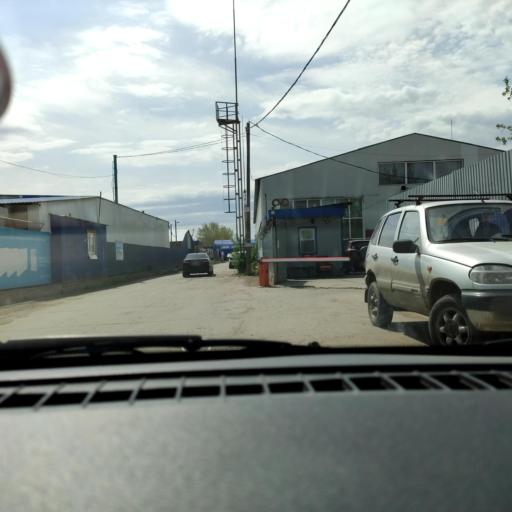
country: RU
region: Samara
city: Samara
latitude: 53.1758
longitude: 50.1234
